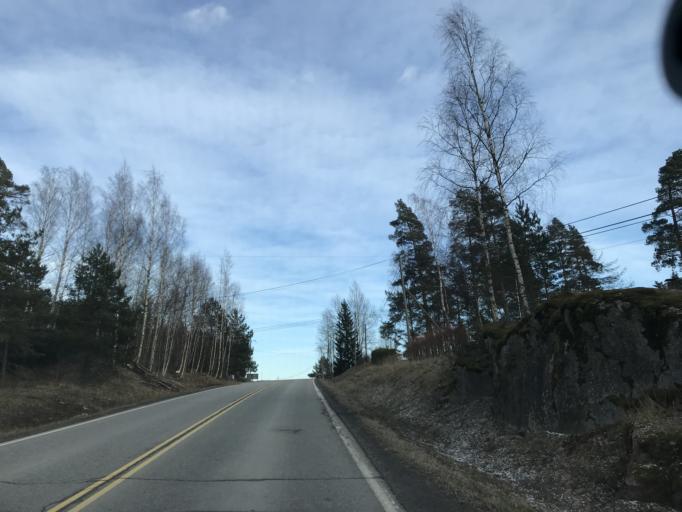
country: FI
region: Uusimaa
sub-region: Raaseporin
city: Pohja
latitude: 60.0917
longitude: 23.4836
